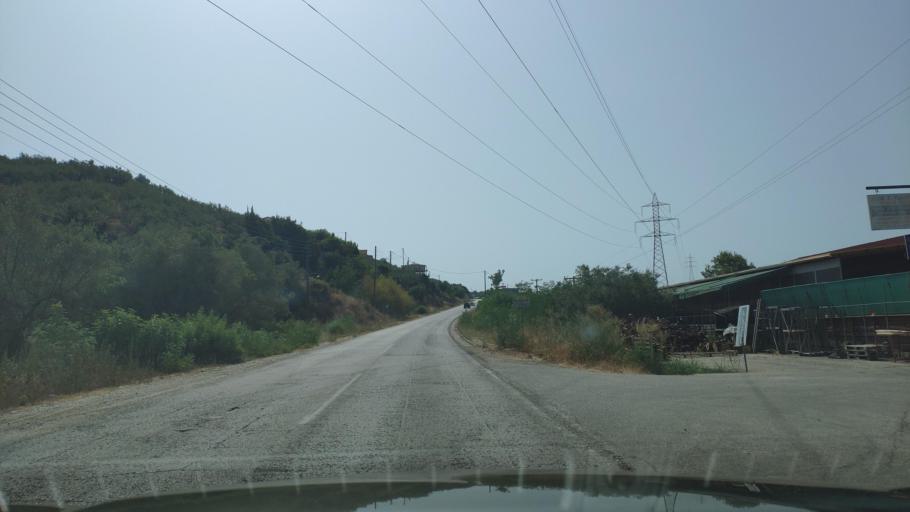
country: GR
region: Epirus
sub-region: Nomos Artas
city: Peta
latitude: 39.1601
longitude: 21.0230
